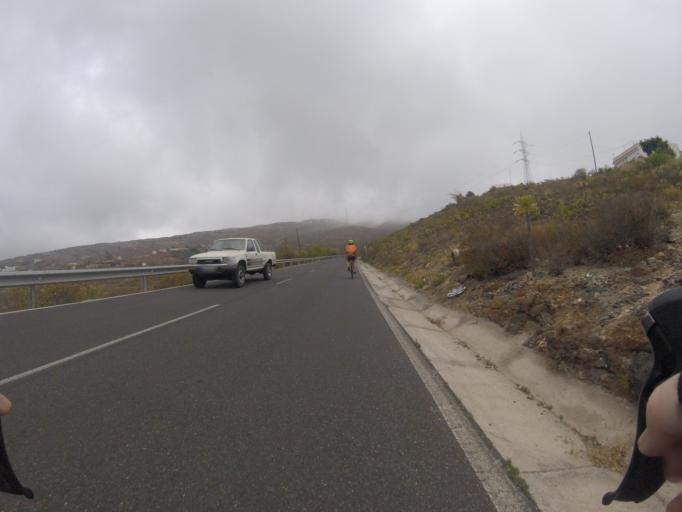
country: ES
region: Canary Islands
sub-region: Provincia de Santa Cruz de Tenerife
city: Guimar
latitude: 28.2893
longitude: -16.4022
